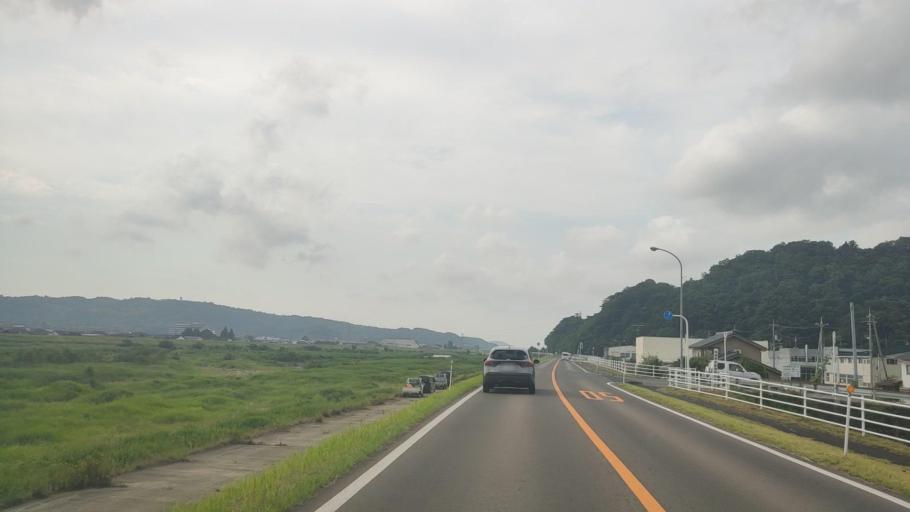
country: JP
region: Tottori
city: Kurayoshi
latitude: 35.4269
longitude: 133.8505
